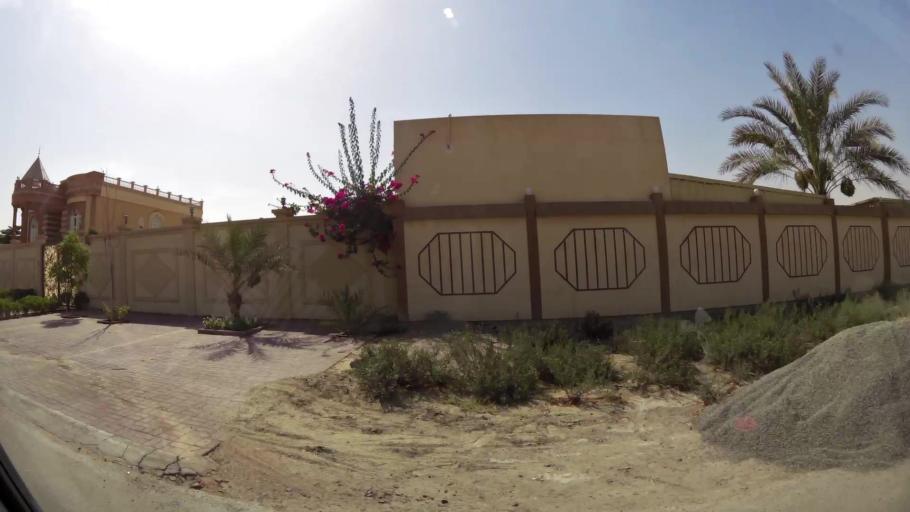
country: AE
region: Ash Shariqah
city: Sharjah
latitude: 25.2658
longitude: 55.4089
